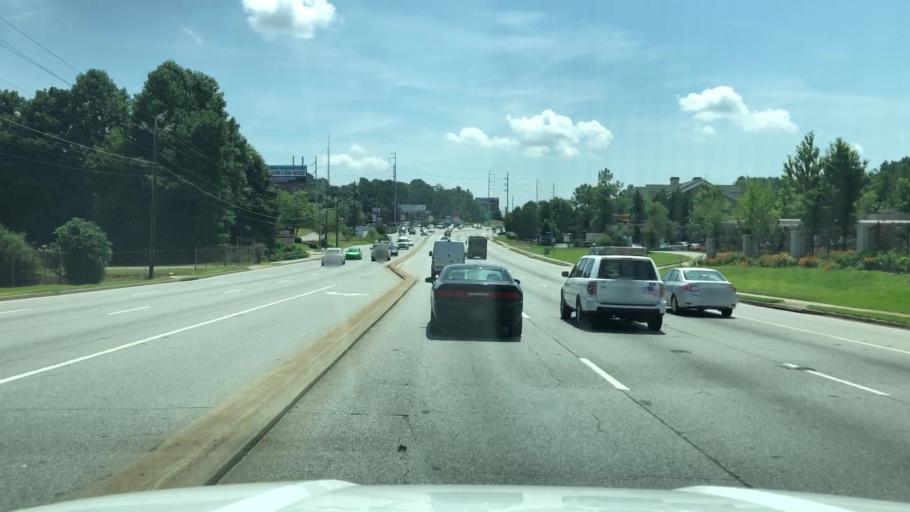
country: US
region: Georgia
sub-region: Gwinnett County
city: Norcross
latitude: 33.9235
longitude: -84.2146
